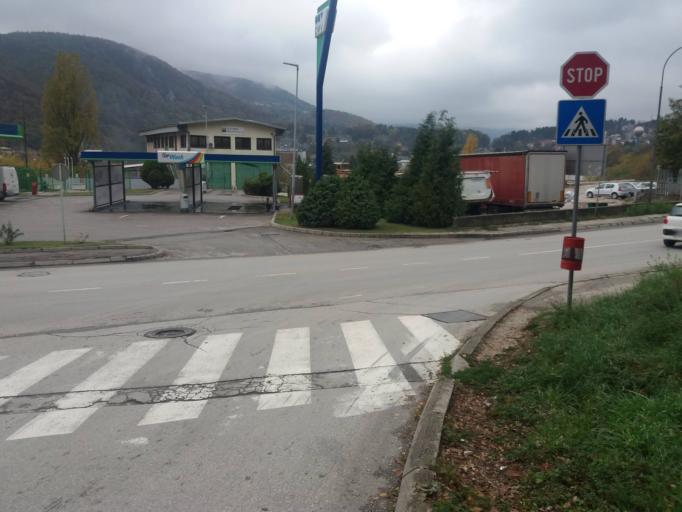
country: RS
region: Central Serbia
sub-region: Zlatiborski Okrug
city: Uzice
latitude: 43.8485
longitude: 19.8634
